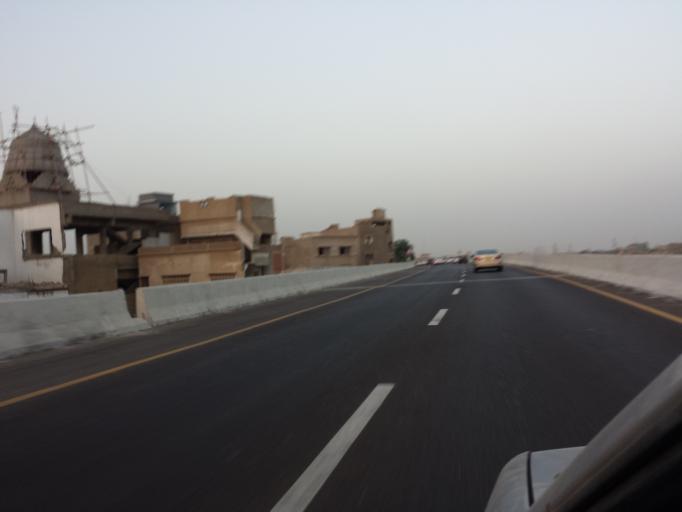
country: PK
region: Sindh
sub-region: Karachi District
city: Karachi
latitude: 24.8988
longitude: 67.0576
